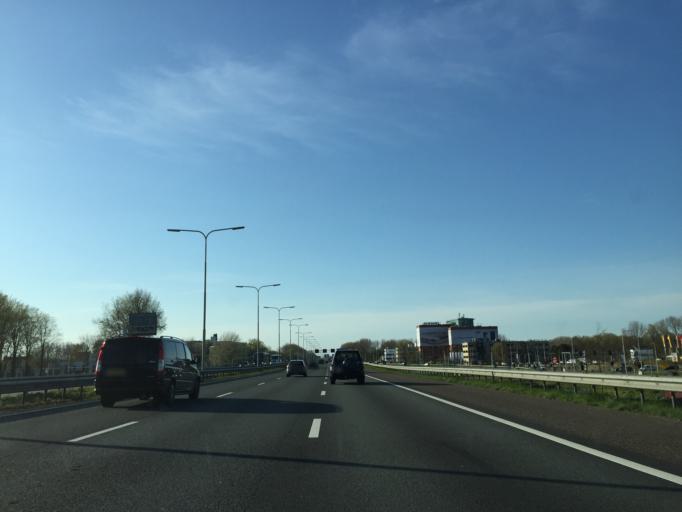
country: NL
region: South Holland
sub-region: Gemeente Delft
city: Delft
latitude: 52.0101
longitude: 4.3796
